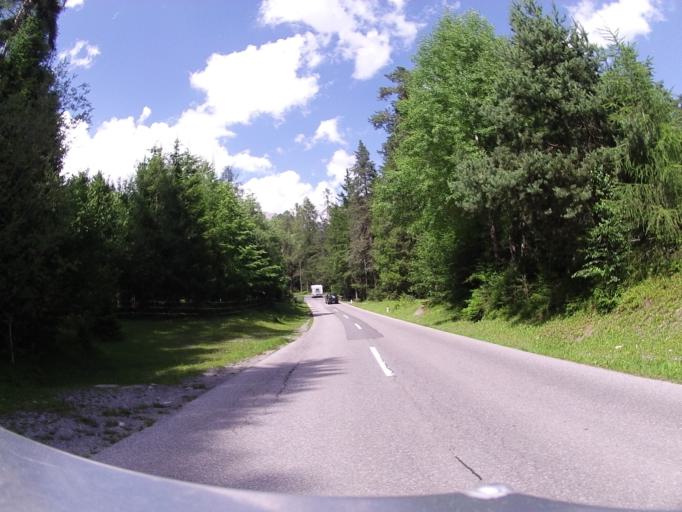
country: AT
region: Tyrol
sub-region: Politischer Bezirk Imst
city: Imst
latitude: 47.2570
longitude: 10.7378
